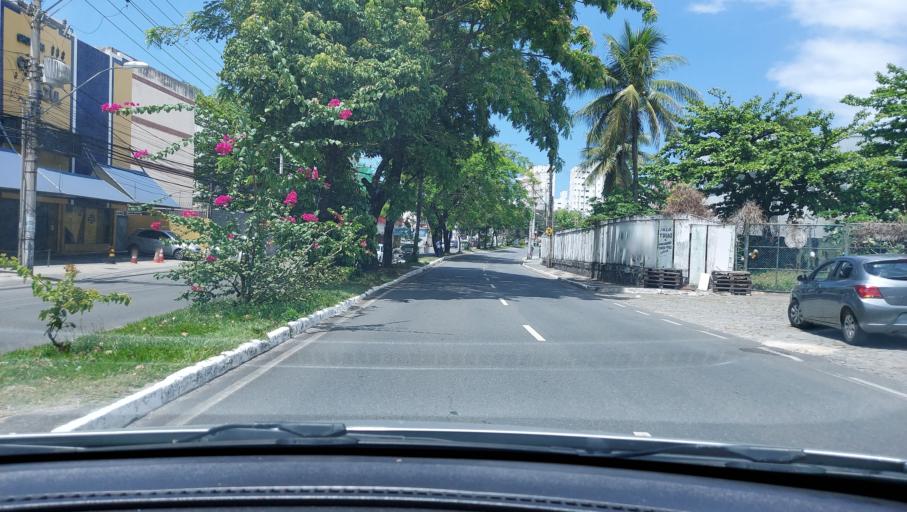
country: BR
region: Bahia
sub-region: Salvador
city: Salvador
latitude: -12.9904
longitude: -38.4479
